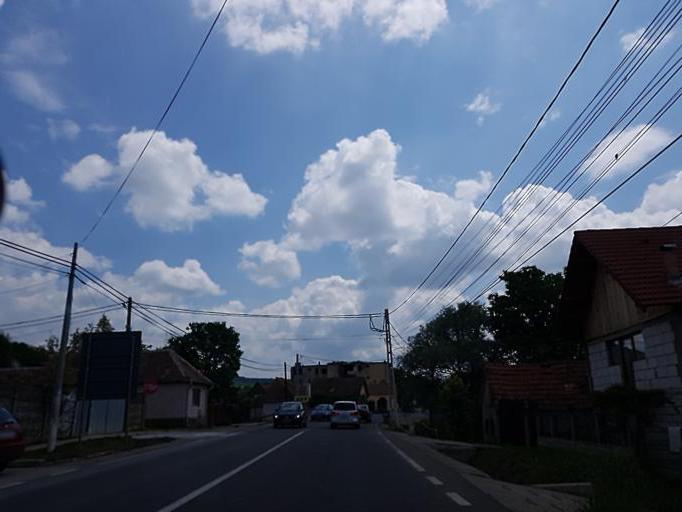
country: RO
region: Sibiu
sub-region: Comuna Slimnic
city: Slimnic
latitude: 45.9639
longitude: 24.1630
